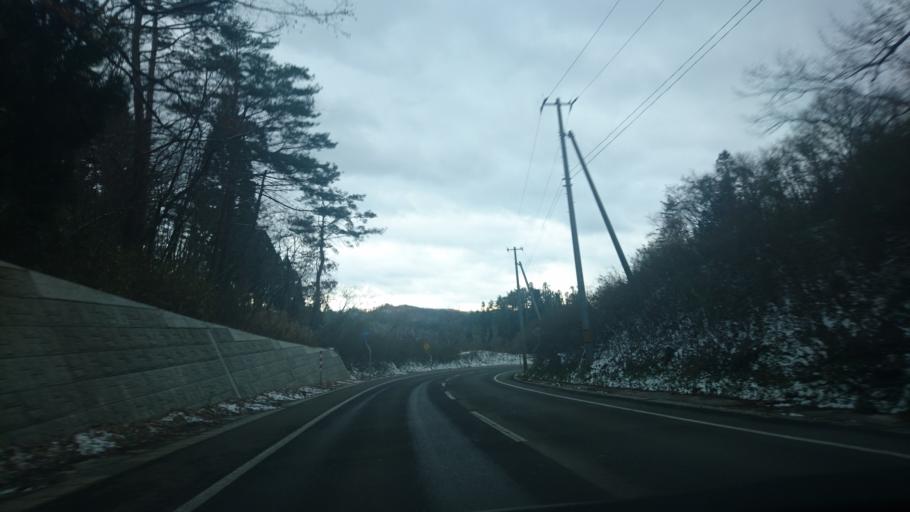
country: JP
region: Iwate
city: Mizusawa
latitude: 39.1587
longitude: 141.2446
